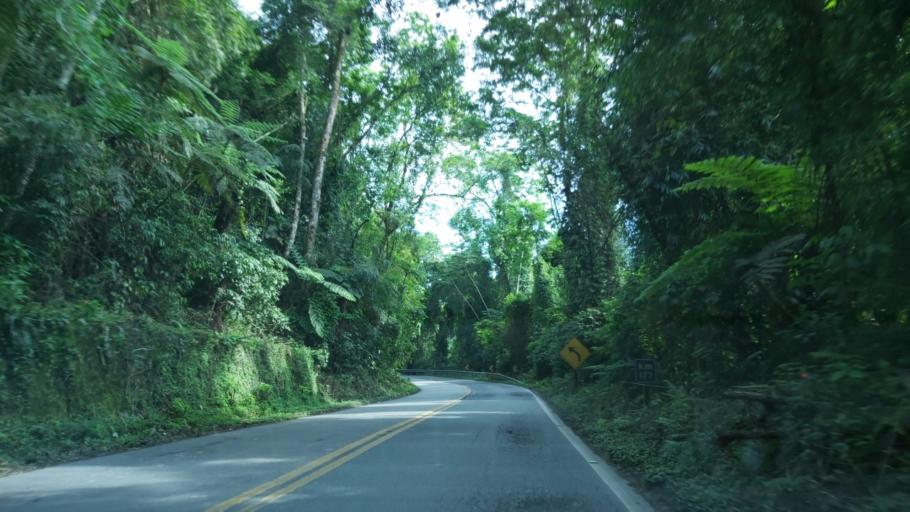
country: BR
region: Sao Paulo
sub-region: Juquia
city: Juquia
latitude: -24.0912
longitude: -47.6157
